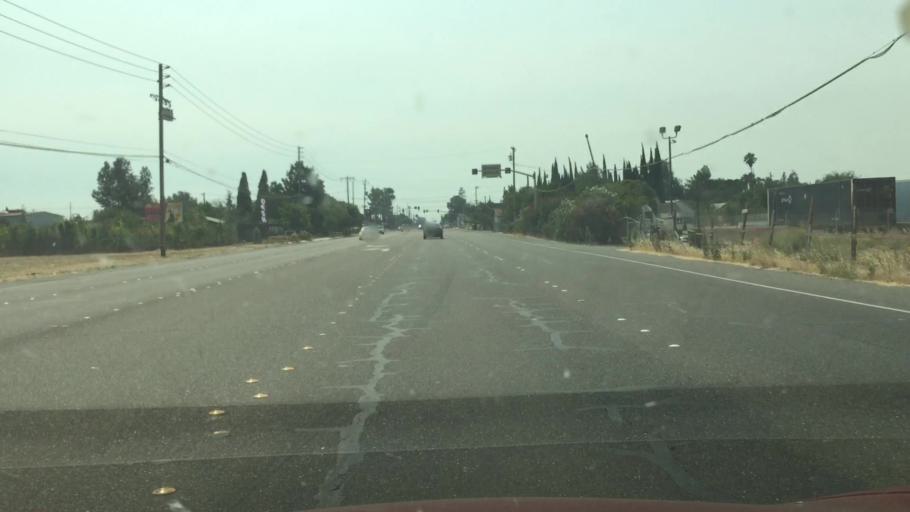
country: US
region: California
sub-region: San Joaquin County
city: Manteca
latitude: 37.7974
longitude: -121.2484
